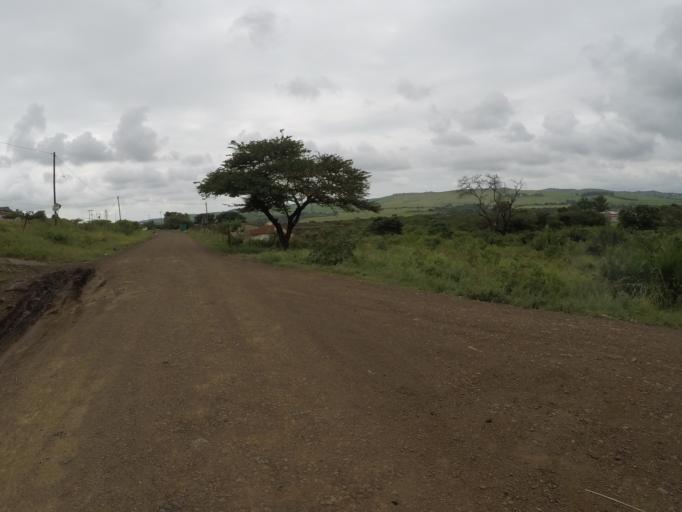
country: ZA
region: KwaZulu-Natal
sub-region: uThungulu District Municipality
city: Empangeni
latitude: -28.7097
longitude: 31.8495
